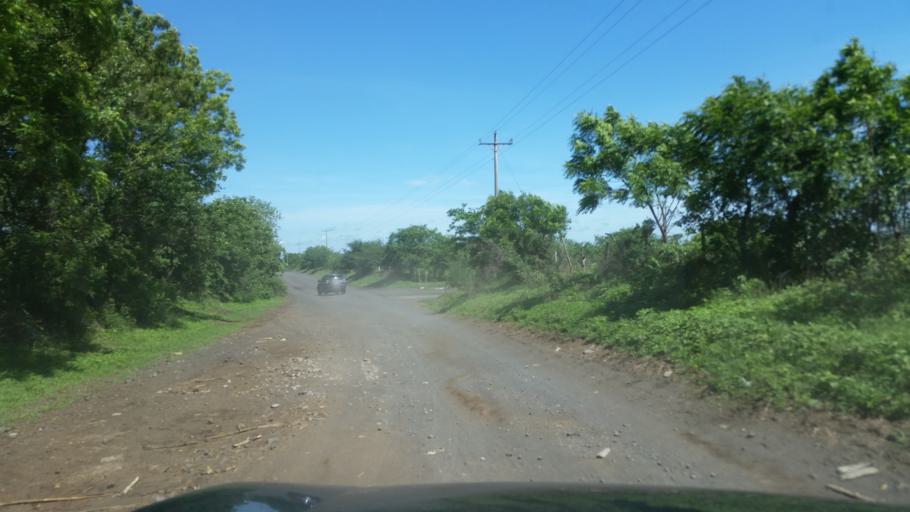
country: NI
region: Chinandega
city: Puerto Morazan
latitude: 12.7683
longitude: -87.0652
